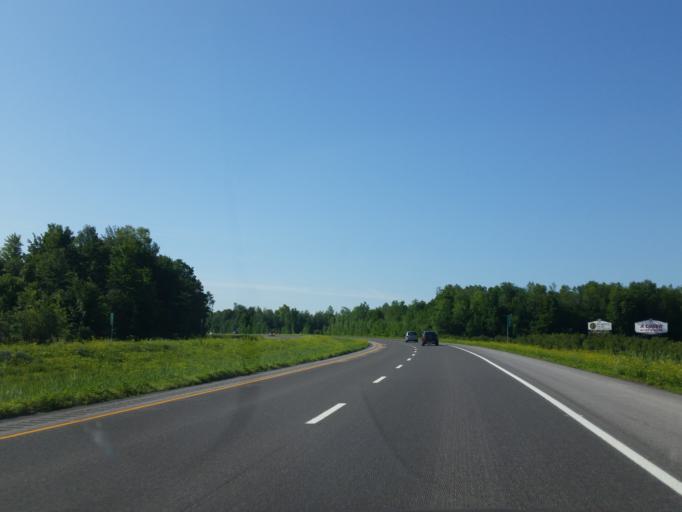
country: CA
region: Quebec
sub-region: Monteregie
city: Napierville
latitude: 45.2165
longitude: -73.4777
